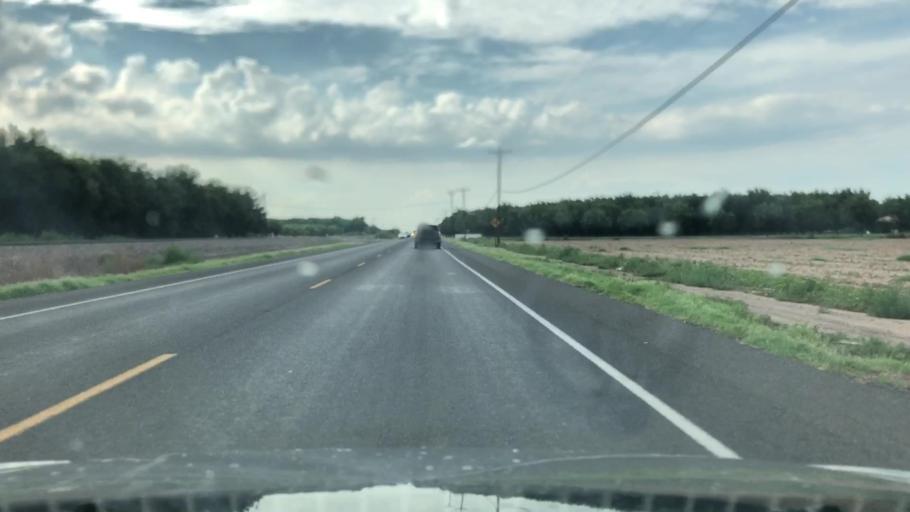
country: US
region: New Mexico
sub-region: Dona Ana County
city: San Miguel
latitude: 32.2190
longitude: -106.7309
